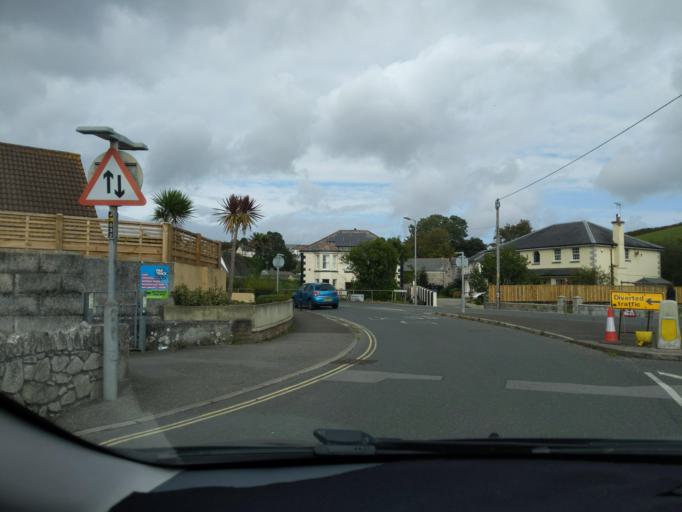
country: GB
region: England
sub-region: Cornwall
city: Par
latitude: 50.3537
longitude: -4.7007
